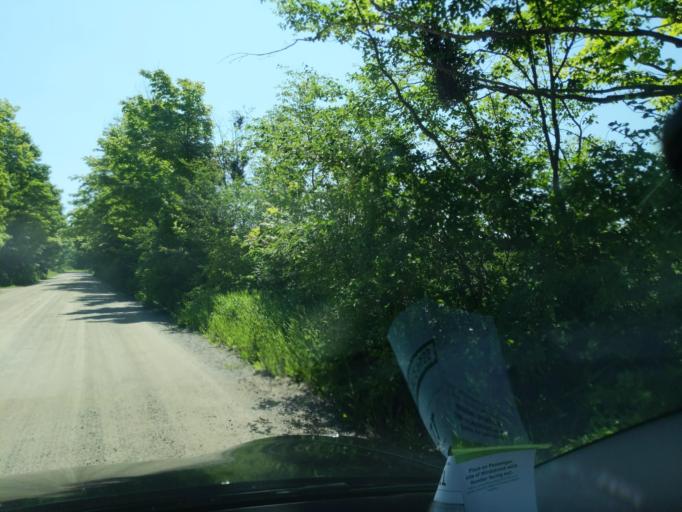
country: US
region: Michigan
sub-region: Cheboygan County
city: Cheboygan
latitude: 45.6536
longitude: -84.6330
